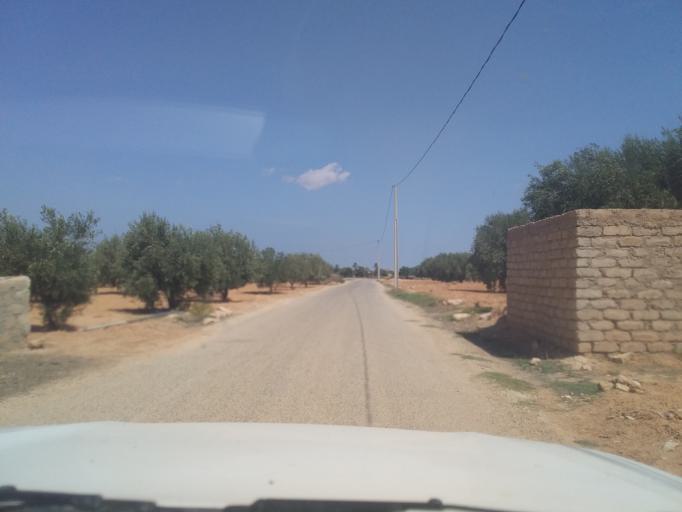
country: TN
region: Qabis
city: Matmata
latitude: 33.5907
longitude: 10.2842
